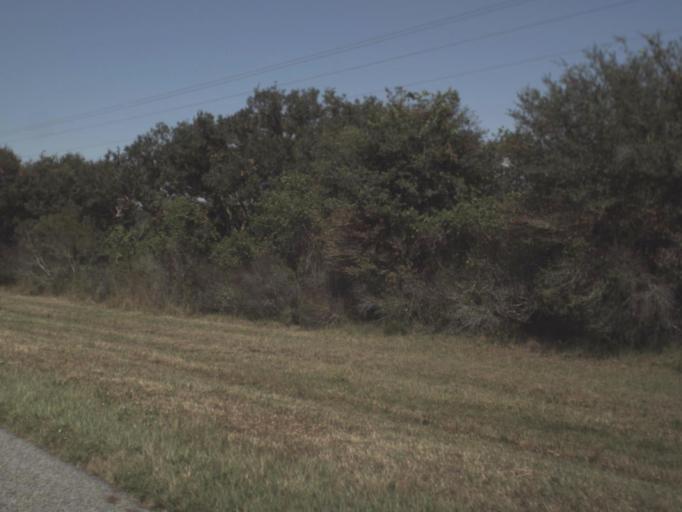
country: US
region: Florida
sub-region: Hendry County
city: Port LaBelle
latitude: 26.9939
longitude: -81.3267
